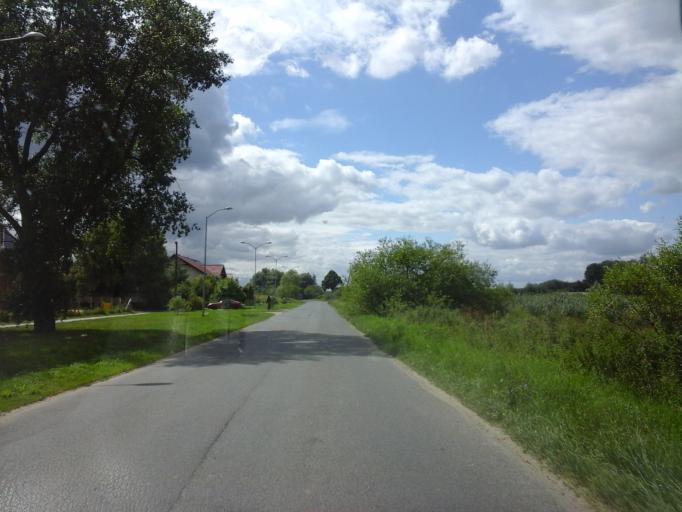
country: PL
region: West Pomeranian Voivodeship
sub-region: Powiat policki
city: Przeclaw
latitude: 53.4217
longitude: 14.4456
